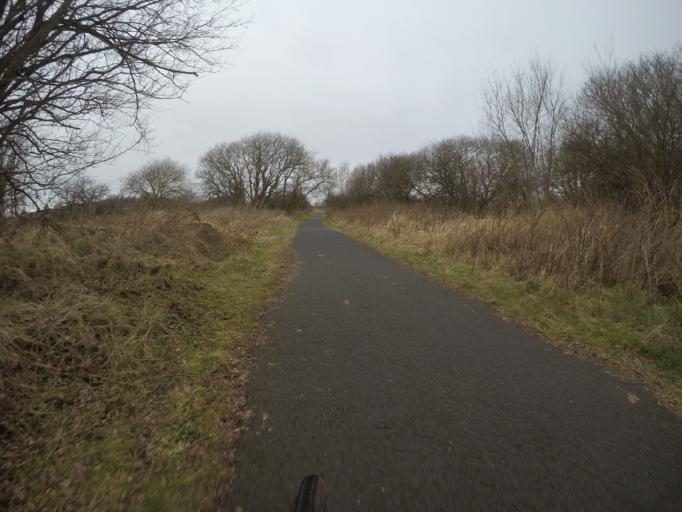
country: GB
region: Scotland
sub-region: North Ayrshire
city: Kilwinning
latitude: 55.6311
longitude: -4.6900
